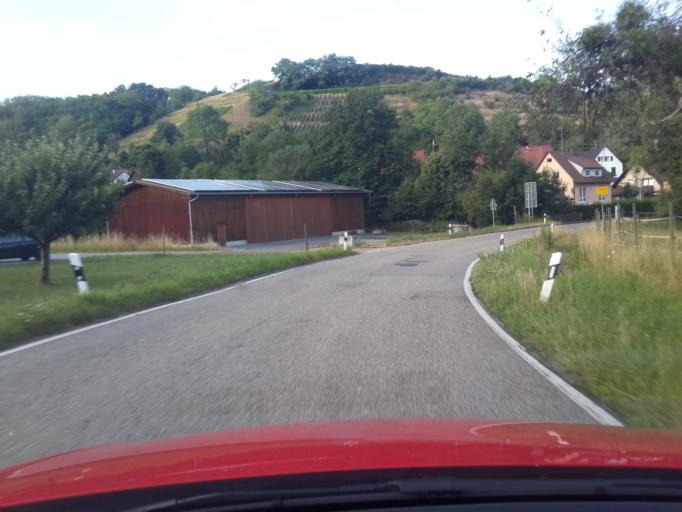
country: DE
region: Baden-Wuerttemberg
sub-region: Regierungsbezirk Stuttgart
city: Pfaffenhofen
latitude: 49.0219
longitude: 8.9763
